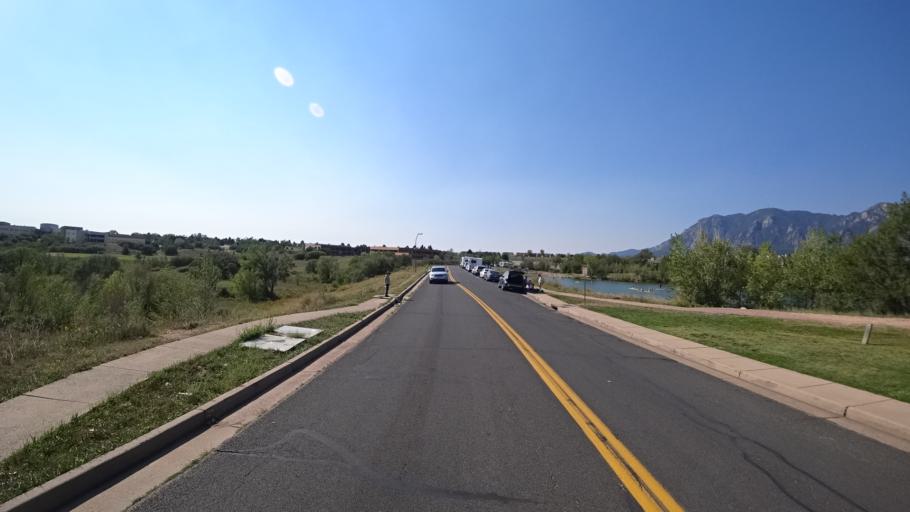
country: US
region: Colorado
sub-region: El Paso County
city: Stratmoor
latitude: 38.7862
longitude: -104.8057
